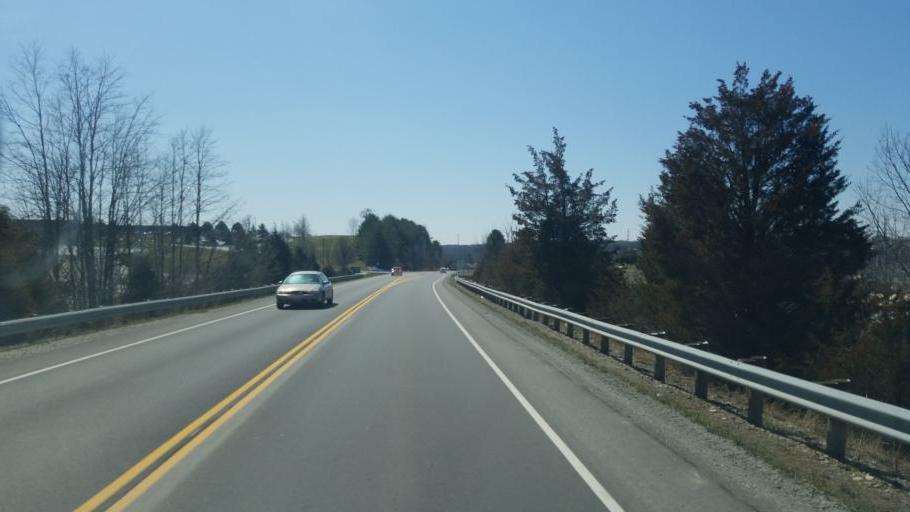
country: US
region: Ohio
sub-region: Highland County
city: Hillsboro
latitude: 39.1911
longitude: -83.6144
